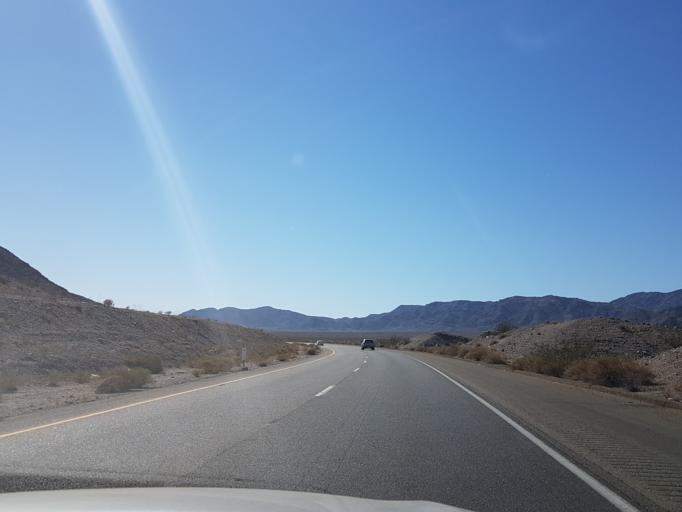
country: US
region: California
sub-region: San Bernardino County
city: Fort Irwin
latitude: 35.1944
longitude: -116.1521
